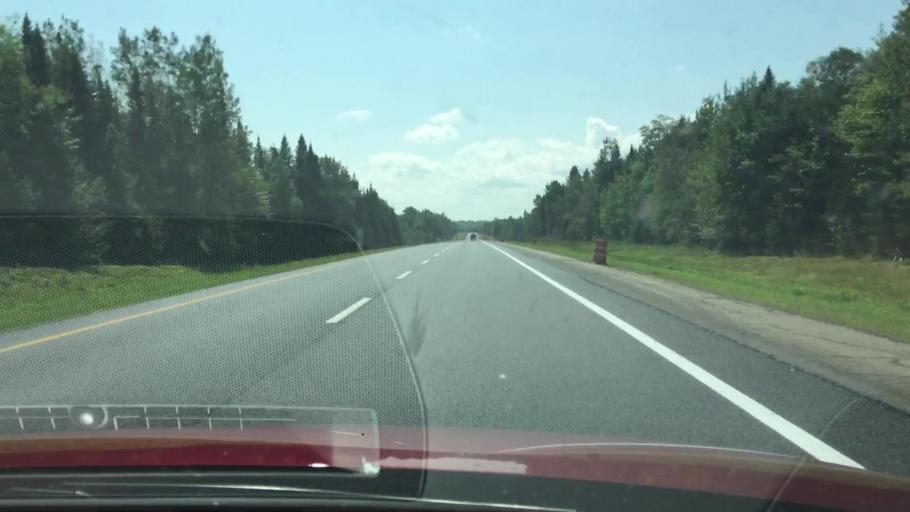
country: US
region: Maine
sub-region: Penobscot County
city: Patten
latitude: 45.8550
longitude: -68.4251
